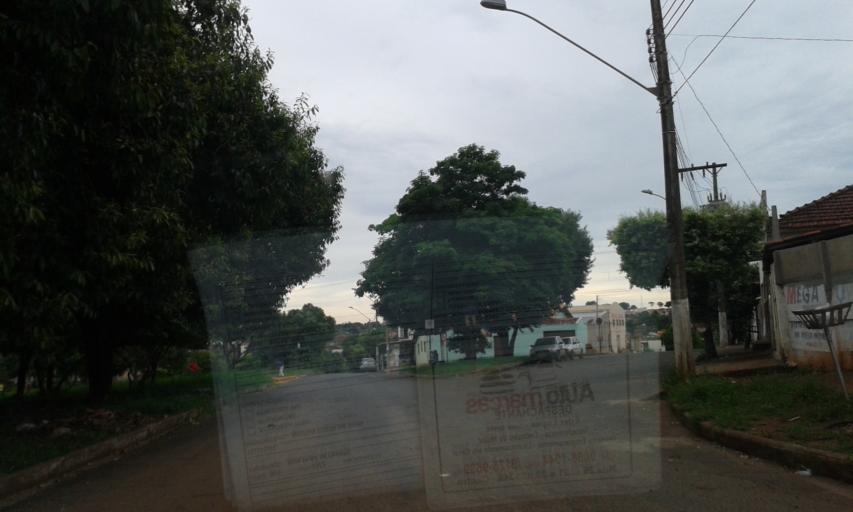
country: BR
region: Minas Gerais
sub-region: Ituiutaba
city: Ituiutaba
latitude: -18.9799
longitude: -49.4498
